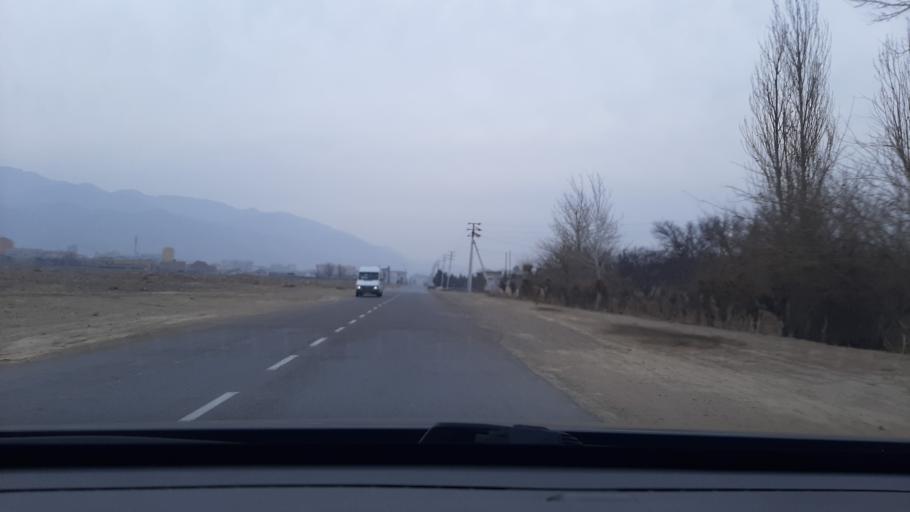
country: TJ
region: Viloyati Sughd
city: Khujand
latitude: 40.2735
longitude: 69.5773
